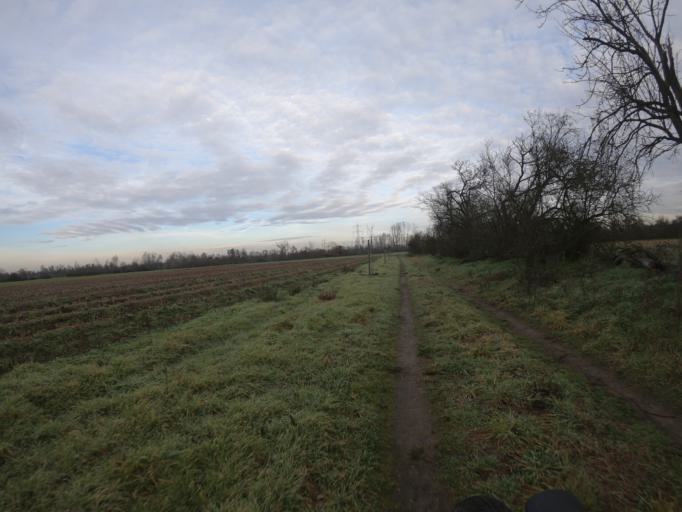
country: DE
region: Hesse
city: Morfelden-Walldorf
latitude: 49.9725
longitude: 8.5856
